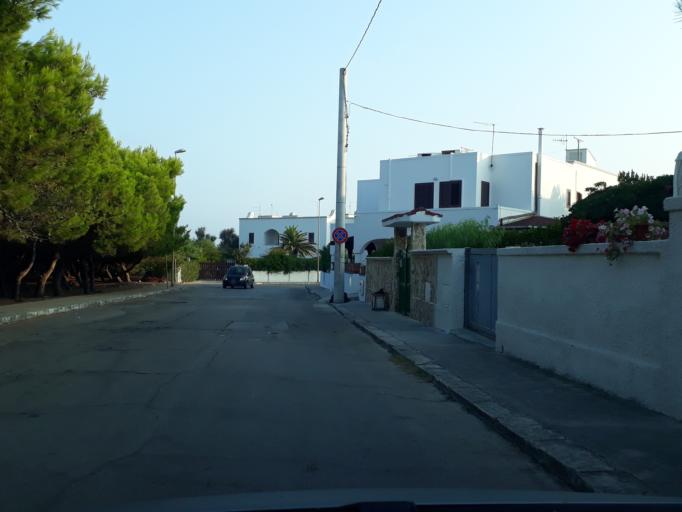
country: IT
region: Apulia
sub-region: Provincia di Brindisi
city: Carovigno
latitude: 40.7573
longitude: 17.7003
